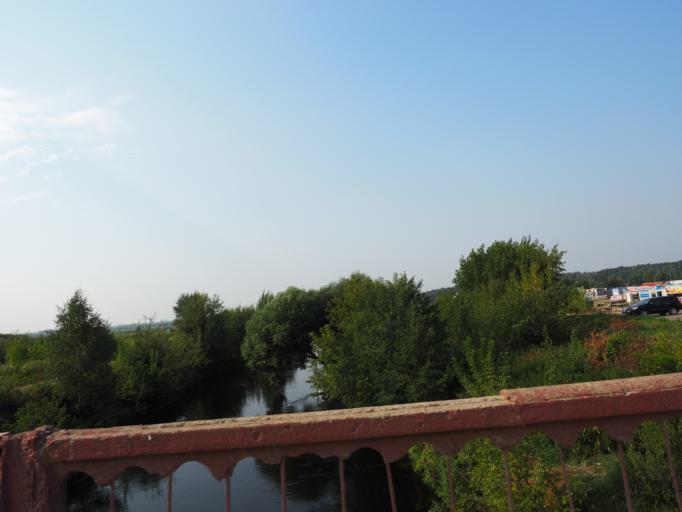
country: RU
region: Moskovskaya
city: Oktyabr'skiy
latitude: 55.6153
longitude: 37.9871
